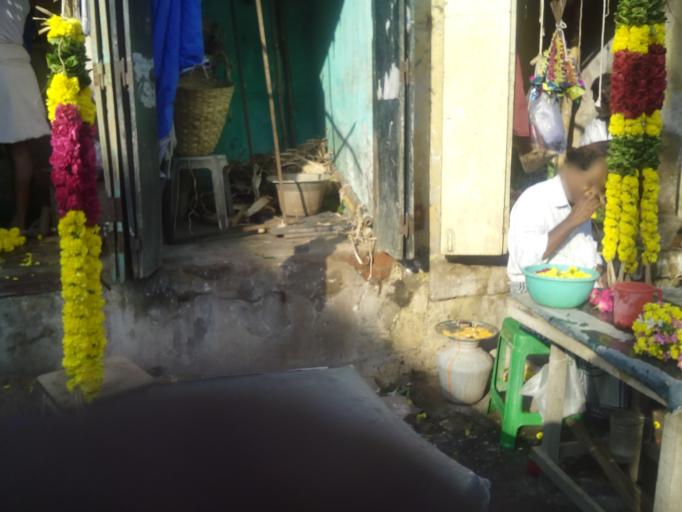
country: IN
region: Tamil Nadu
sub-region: Thanjavur
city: Kumbakonam
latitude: 10.9596
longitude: 79.3733
